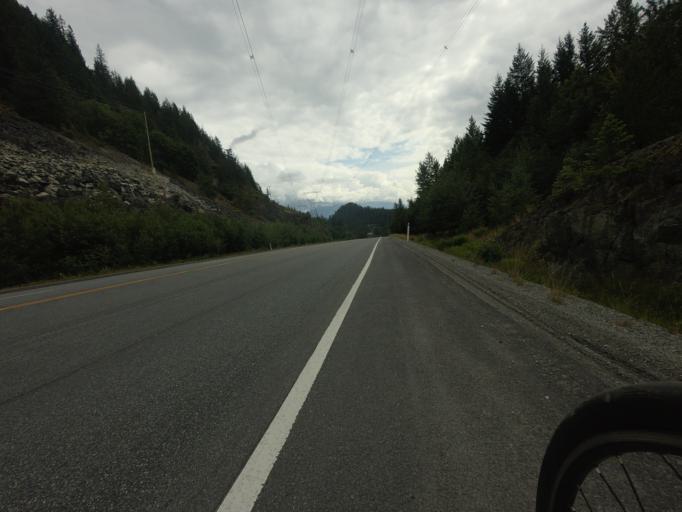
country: CA
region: British Columbia
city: Whistler
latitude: 49.8321
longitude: -123.1353
